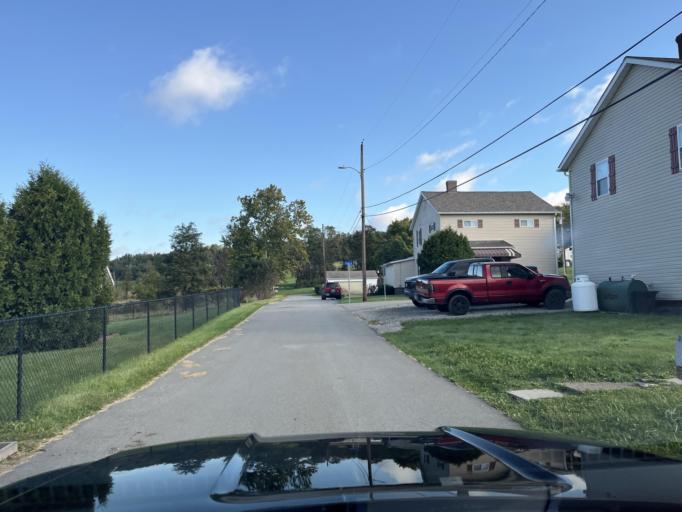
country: US
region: Pennsylvania
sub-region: Fayette County
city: South Uniontown
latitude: 39.8789
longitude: -79.7672
